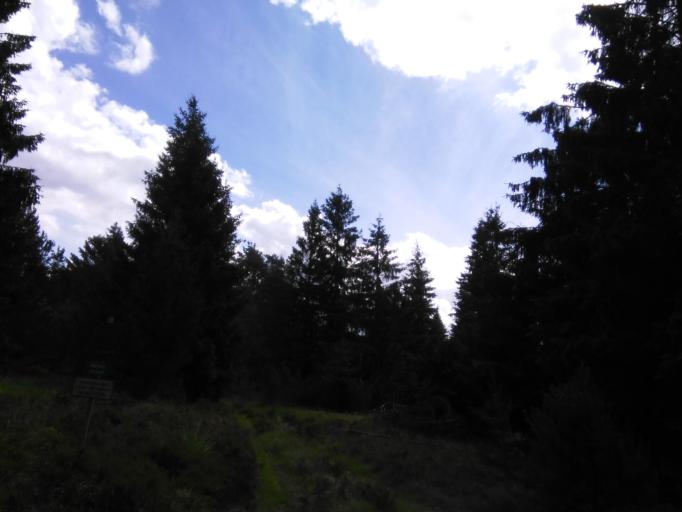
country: DK
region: Central Jutland
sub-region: Silkeborg Kommune
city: Virklund
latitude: 56.0815
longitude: 9.4328
